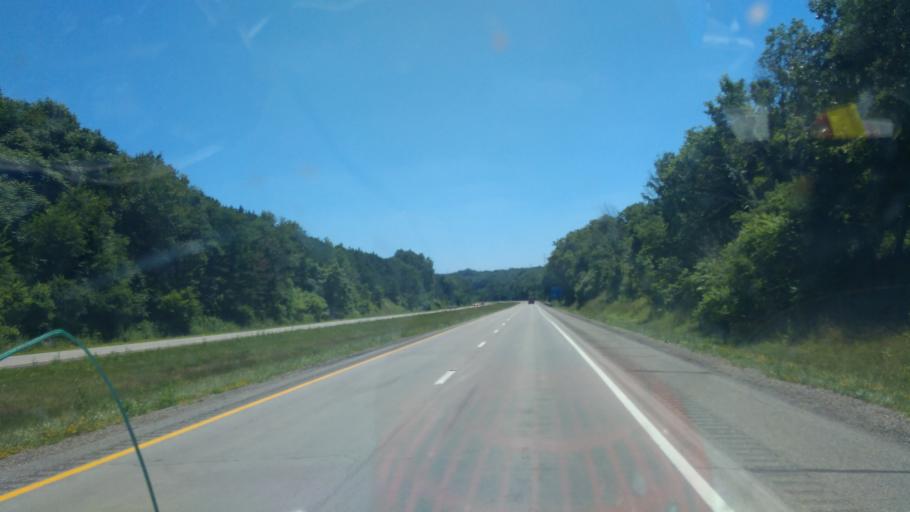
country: US
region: Ohio
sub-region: Columbiana County
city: Lisbon
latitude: 40.7758
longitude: -80.7343
